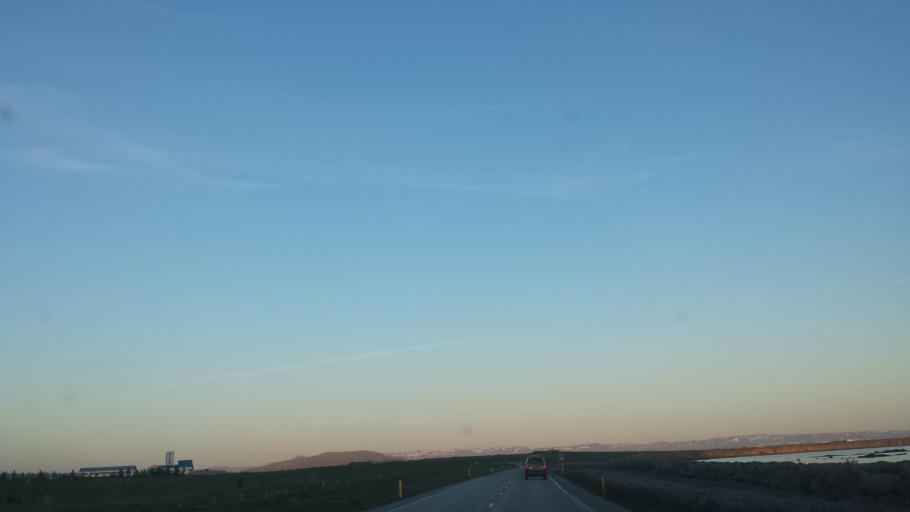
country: IS
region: Capital Region
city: Reykjavik
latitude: 64.2314
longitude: -21.8170
